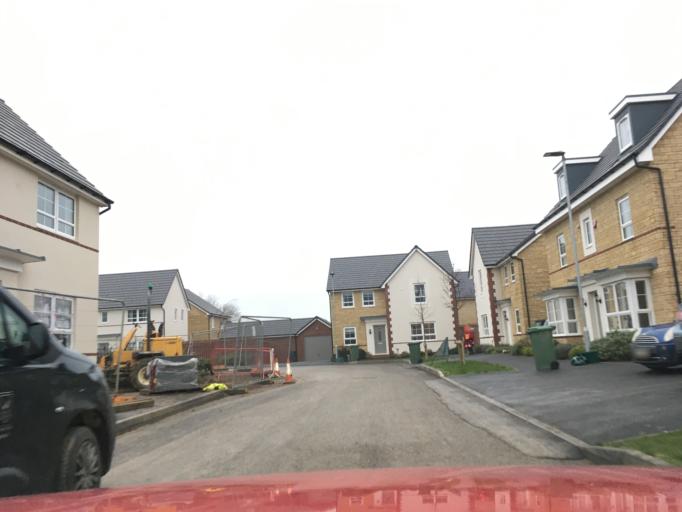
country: GB
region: England
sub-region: Gloucestershire
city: Stonehouse
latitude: 51.7275
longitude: -2.2821
